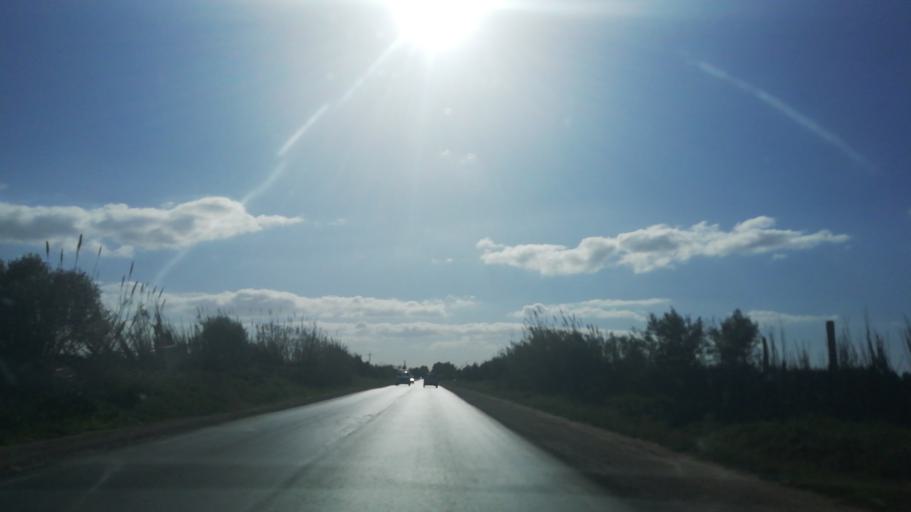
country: DZ
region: Mostaganem
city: Mostaganem
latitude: 35.9671
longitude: 0.2611
